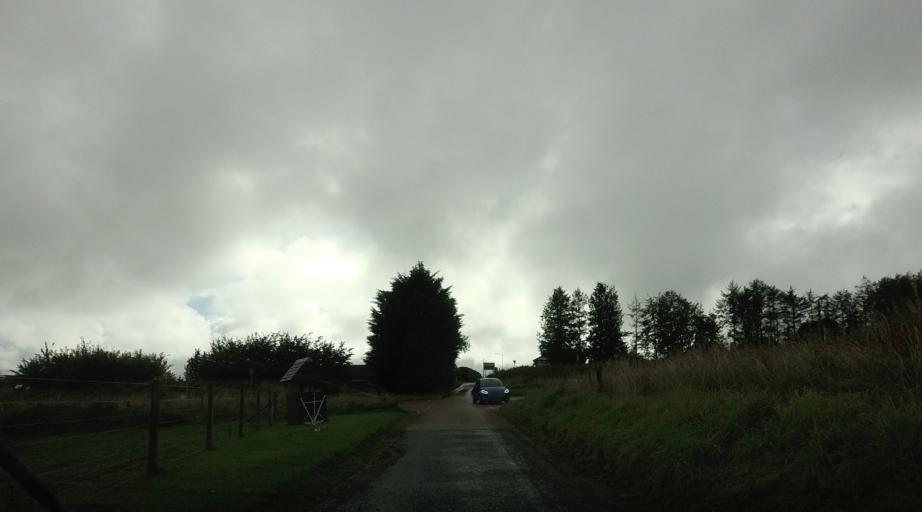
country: GB
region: Scotland
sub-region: Fife
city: Balmullo
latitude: 56.3825
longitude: -2.9288
